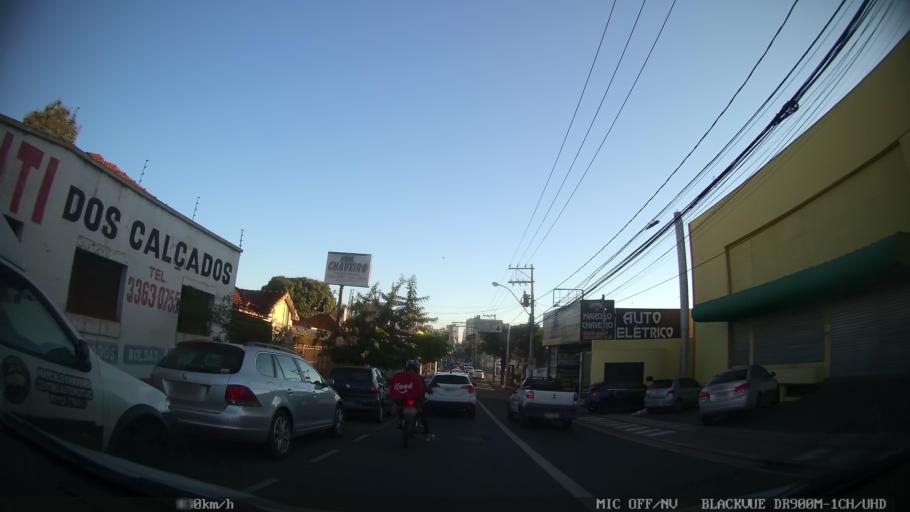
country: BR
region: Sao Paulo
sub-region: Sao Jose Do Rio Preto
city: Sao Jose do Rio Preto
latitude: -20.8059
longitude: -49.3763
